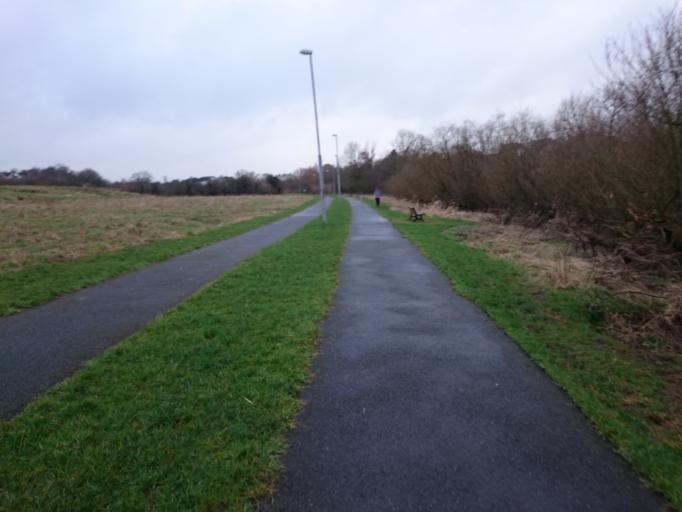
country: IE
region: Leinster
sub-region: Kilkenny
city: Kilkenny
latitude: 52.6622
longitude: -7.2553
